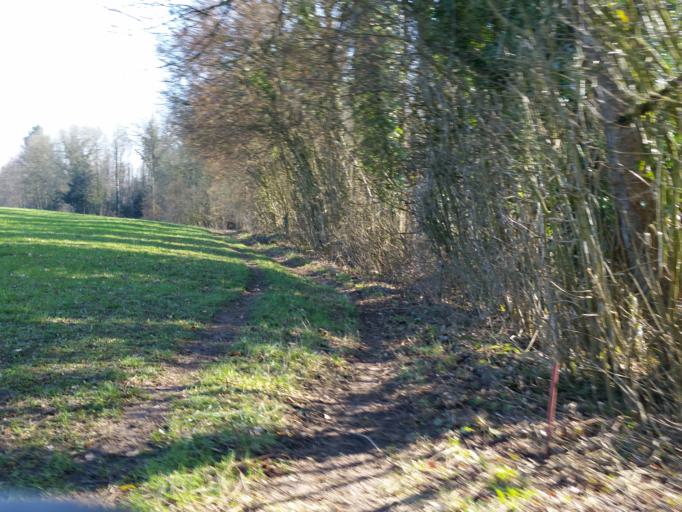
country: CH
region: Thurgau
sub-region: Arbon District
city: Uttwil
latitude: 47.5739
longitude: 9.3435
